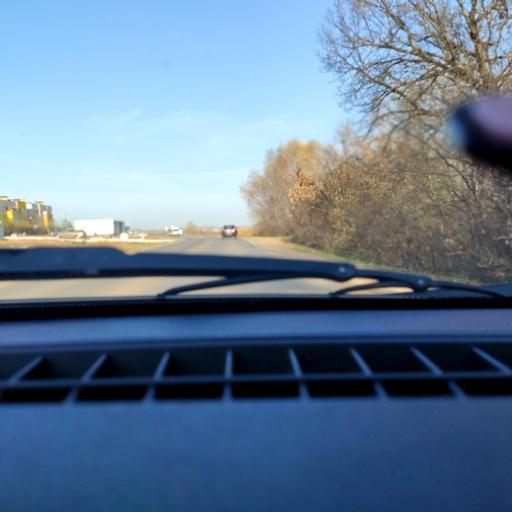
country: RU
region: Bashkortostan
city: Ufa
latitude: 54.7953
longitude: 55.9598
